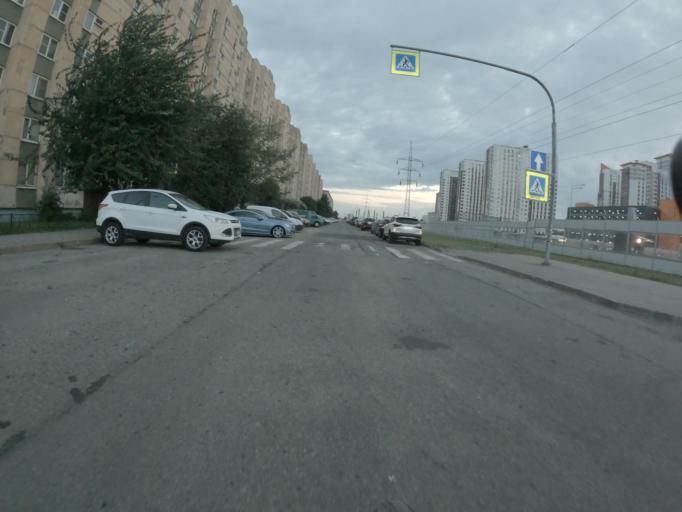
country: RU
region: St.-Petersburg
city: Kupchino
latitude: 59.8301
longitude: 30.3352
